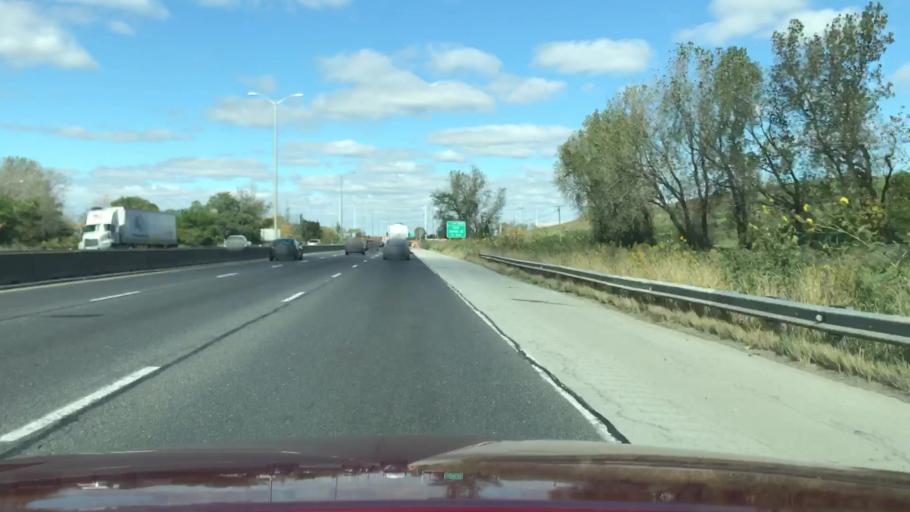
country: US
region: Illinois
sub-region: Cook County
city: Dolton
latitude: 41.6539
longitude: -87.5834
